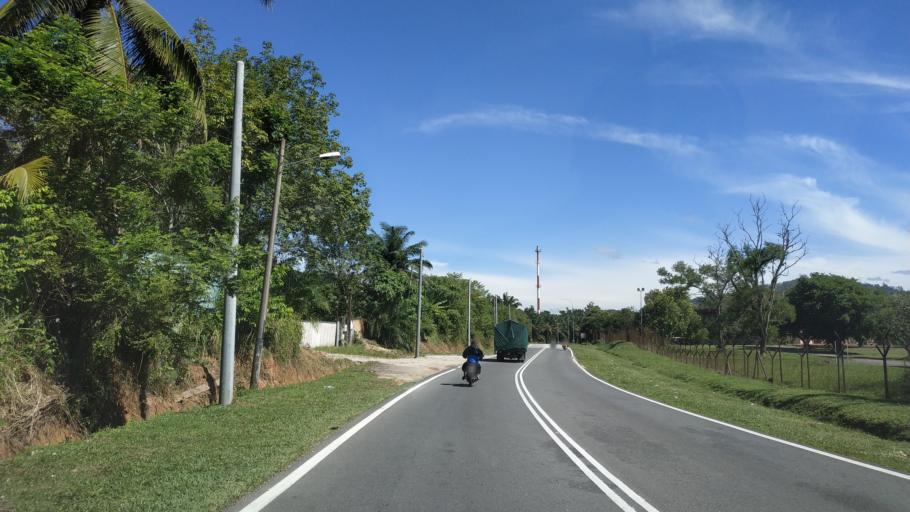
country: MY
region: Kedah
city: Kulim
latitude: 5.3317
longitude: 100.5345
